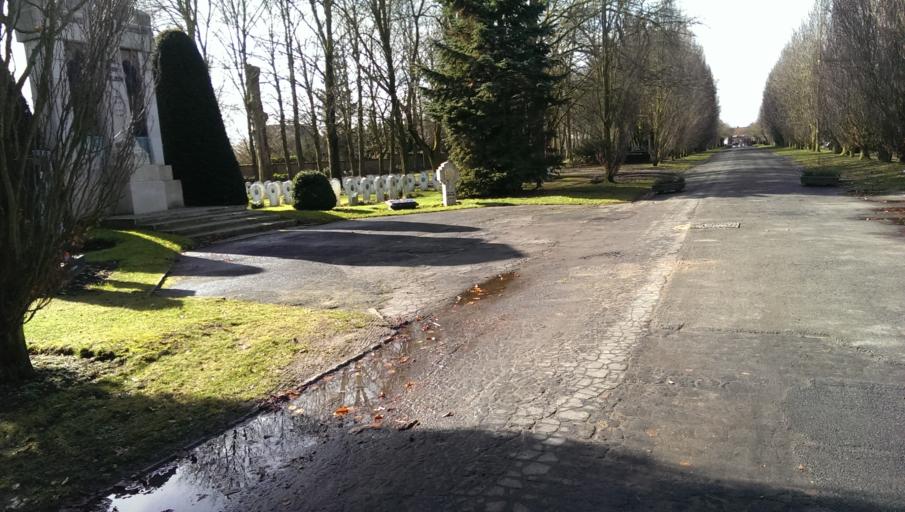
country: BE
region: Flanders
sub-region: Provincie West-Vlaanderen
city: Roeselare
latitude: 50.9434
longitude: 3.1172
